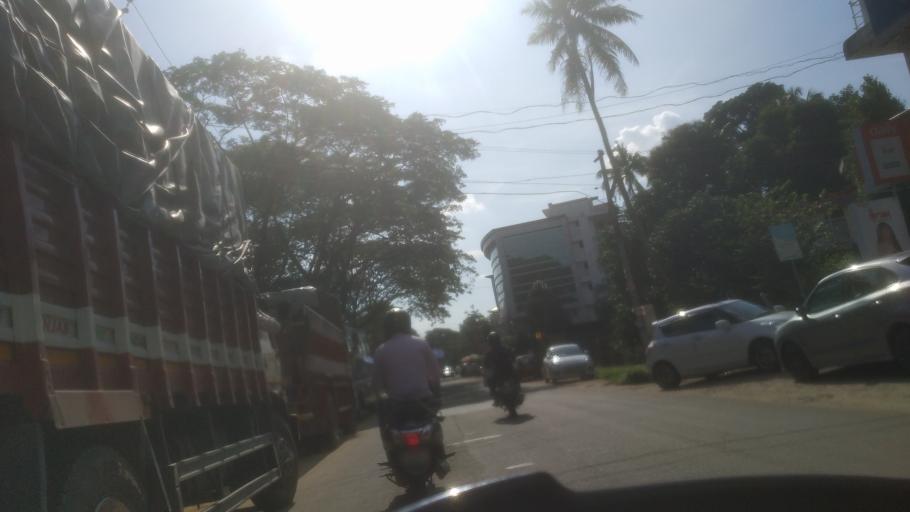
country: IN
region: Kerala
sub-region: Ernakulam
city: Muvattupula
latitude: 9.9912
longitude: 76.5796
